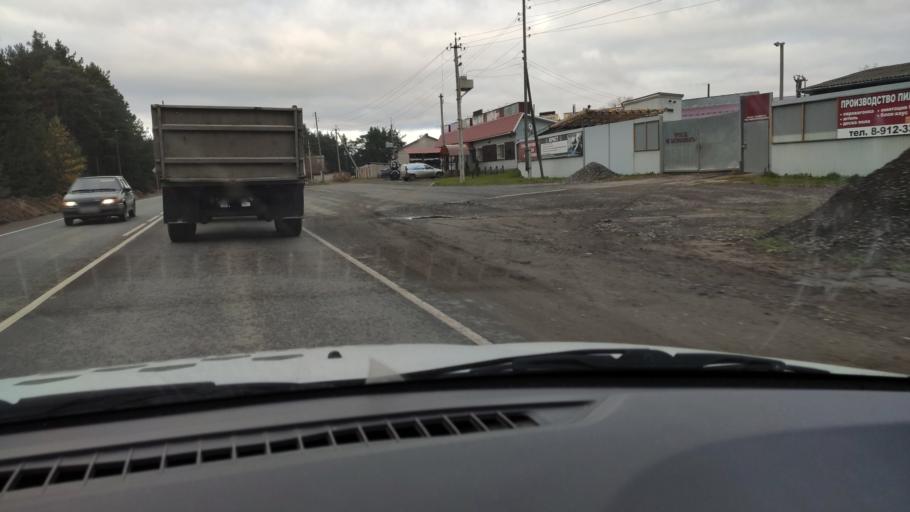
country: RU
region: Kirov
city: Belaya Kholunitsa
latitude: 58.8492
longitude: 50.8274
